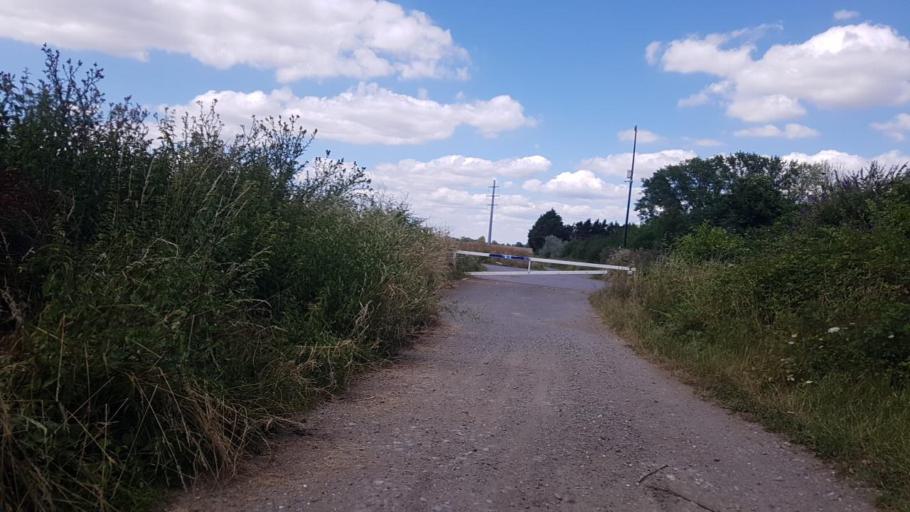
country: FR
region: Ile-de-France
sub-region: Departement de Seine-et-Marne
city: Claye-Souilly
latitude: 48.9764
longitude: 2.6690
